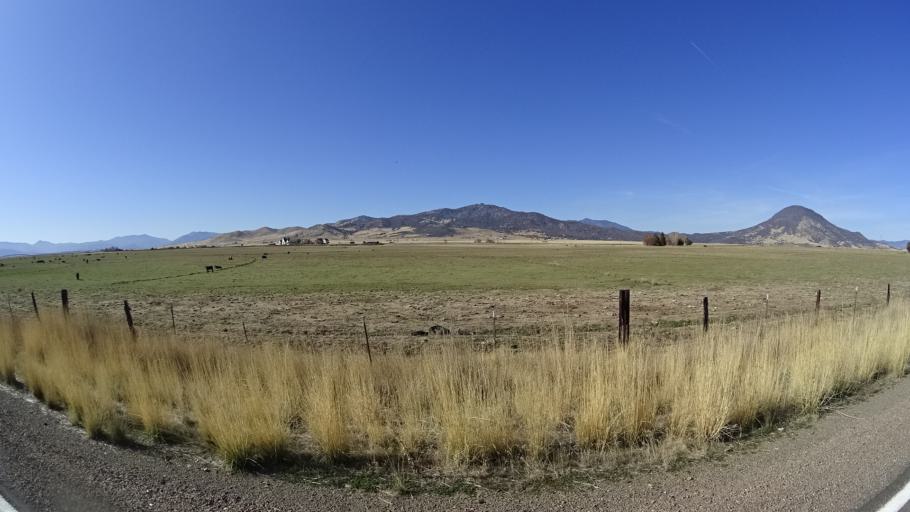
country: US
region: California
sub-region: Siskiyou County
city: Montague
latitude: 41.7908
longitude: -122.4719
